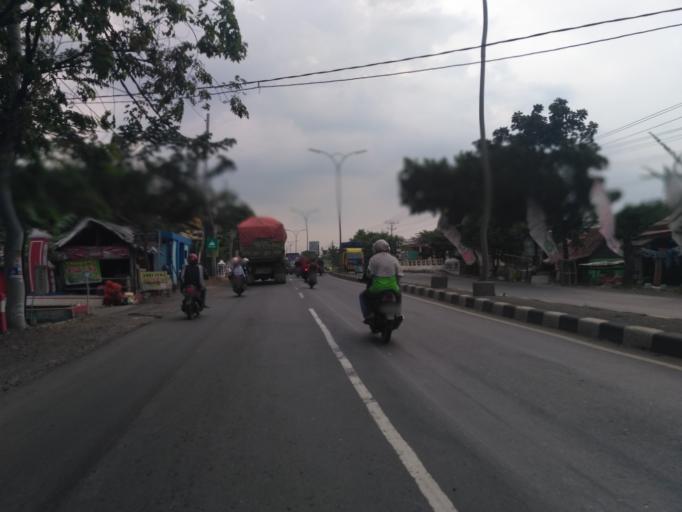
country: ID
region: Central Java
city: Semarang
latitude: -6.9728
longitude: 110.3078
